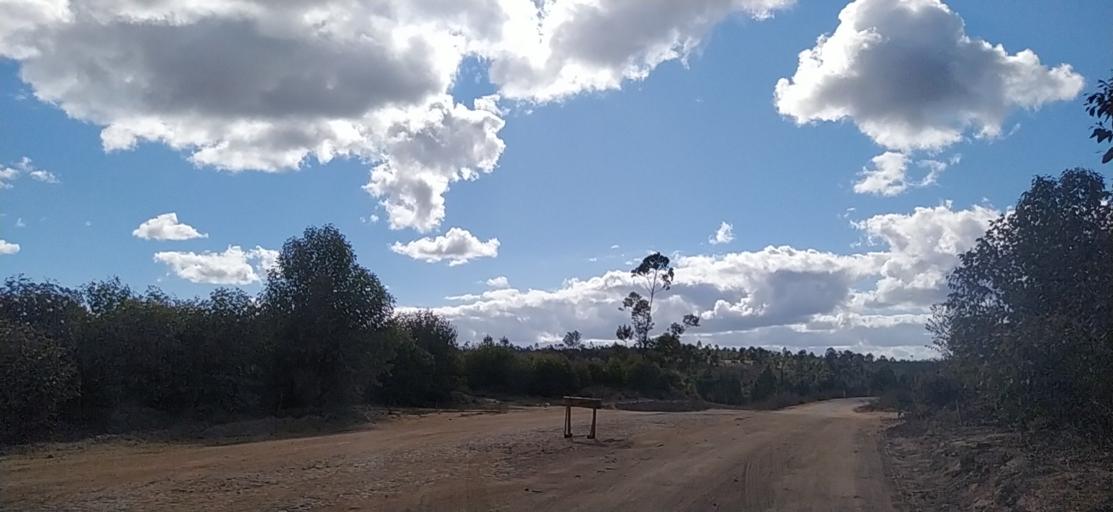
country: MG
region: Alaotra Mangoro
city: Moramanga
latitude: -18.5846
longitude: 48.2725
